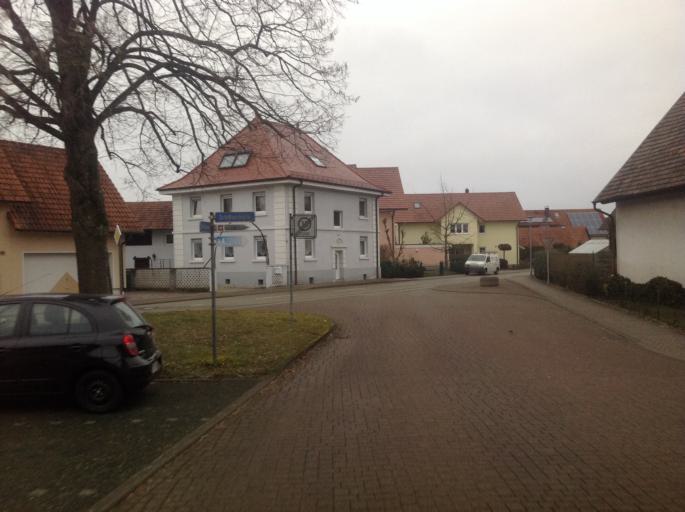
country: DE
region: Baden-Wuerttemberg
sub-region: Karlsruhe Region
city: Iffezheim
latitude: 48.8192
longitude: 8.1426
